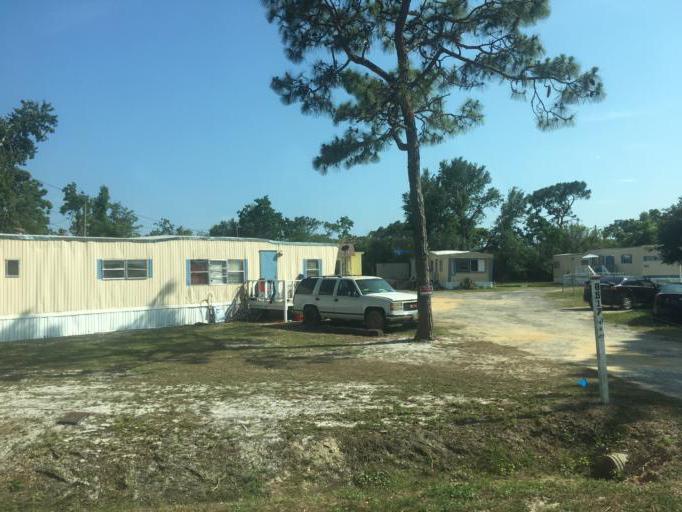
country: US
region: Florida
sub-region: Bay County
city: Panama City Beach
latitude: 30.1749
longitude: -85.7803
